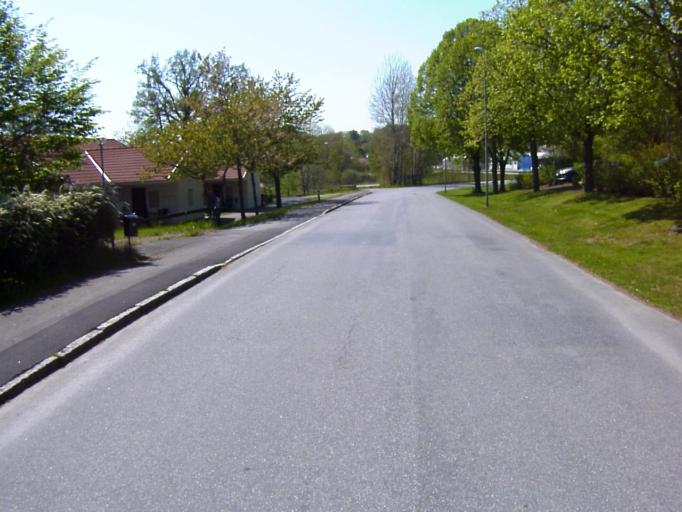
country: SE
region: Skane
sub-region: Kristianstads Kommun
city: Tollarp
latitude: 56.1753
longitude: 14.2891
